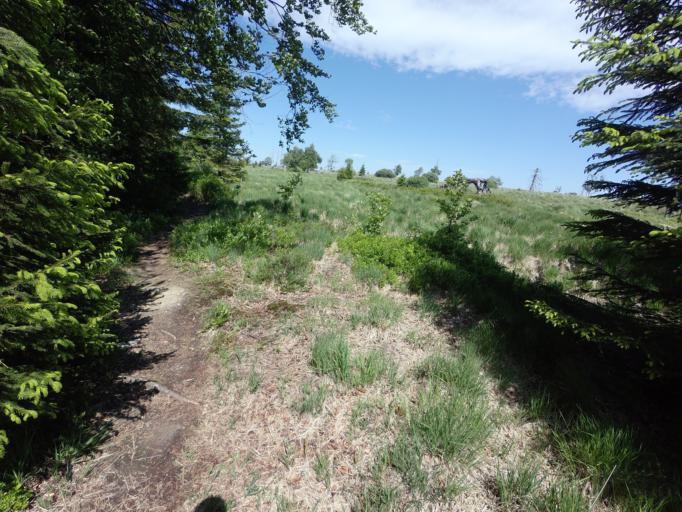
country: BE
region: Wallonia
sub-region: Province de Liege
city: Jalhay
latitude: 50.5134
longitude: 6.0382
